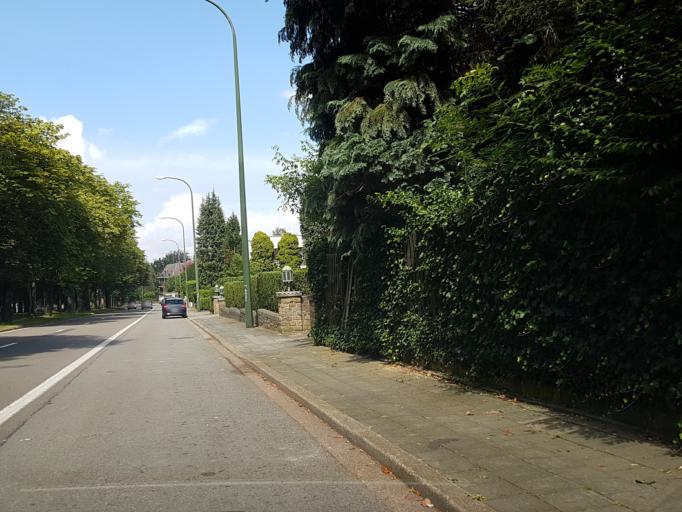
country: BE
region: Flanders
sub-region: Provincie Vlaams-Brabant
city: Kraainem
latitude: 50.8244
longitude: 4.4468
